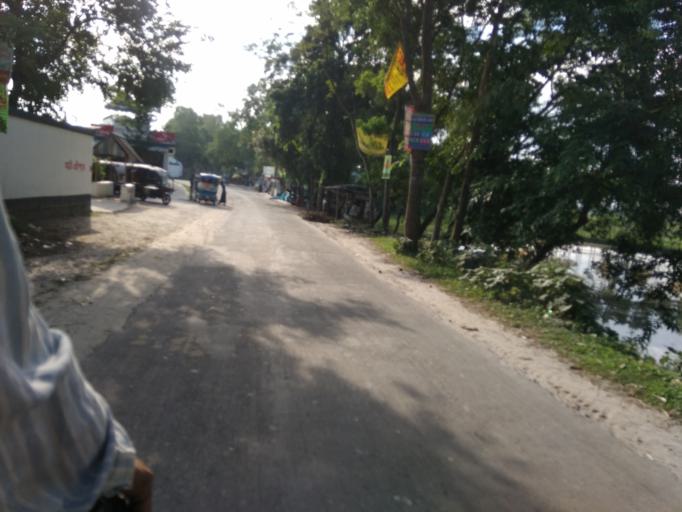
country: BD
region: Rangpur Division
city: Rangpur
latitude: 25.8326
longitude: 89.1126
